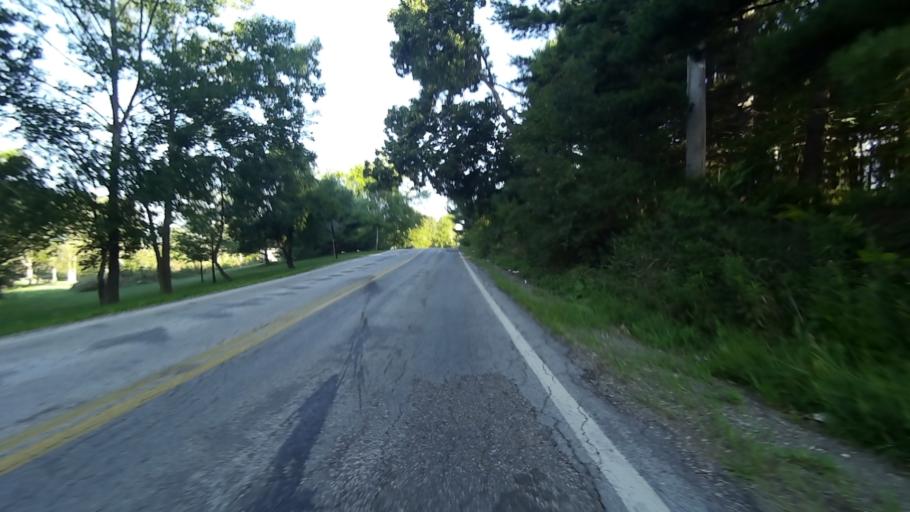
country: US
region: Ohio
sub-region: Portage County
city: Streetsboro
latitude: 41.2028
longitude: -81.3694
